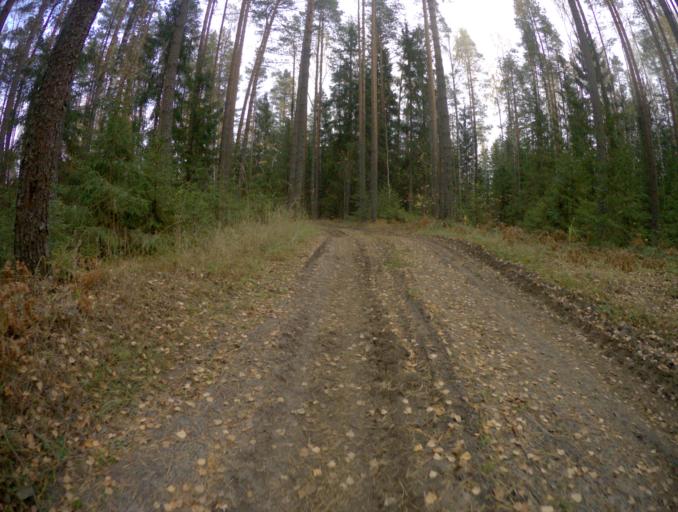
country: RU
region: Vladimir
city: Raduzhnyy
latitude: 55.9306
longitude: 40.3525
